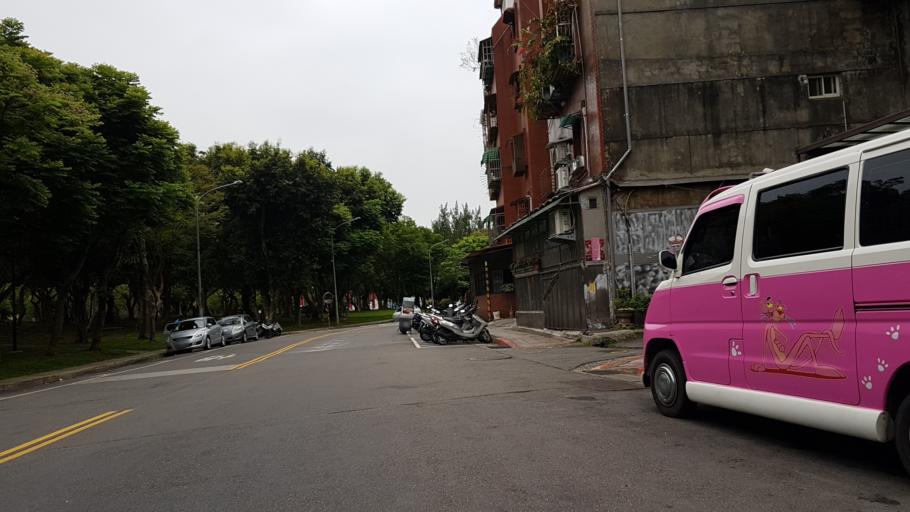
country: TW
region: Taipei
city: Taipei
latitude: 25.0444
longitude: 121.5929
